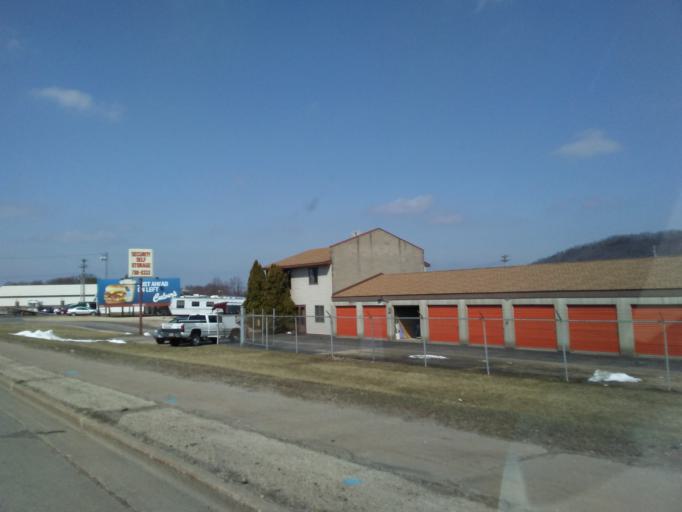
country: US
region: Wisconsin
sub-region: La Crosse County
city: La Crosse
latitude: 43.7639
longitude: -91.2091
